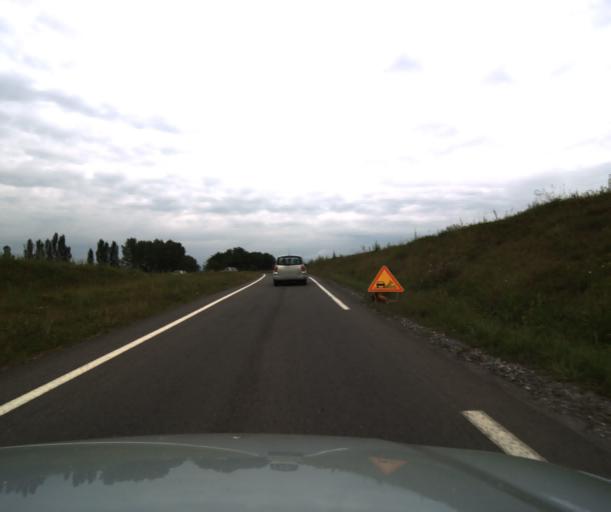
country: FR
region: Midi-Pyrenees
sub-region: Departement des Hautes-Pyrenees
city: Ossun
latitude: 43.1619
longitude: -0.0145
